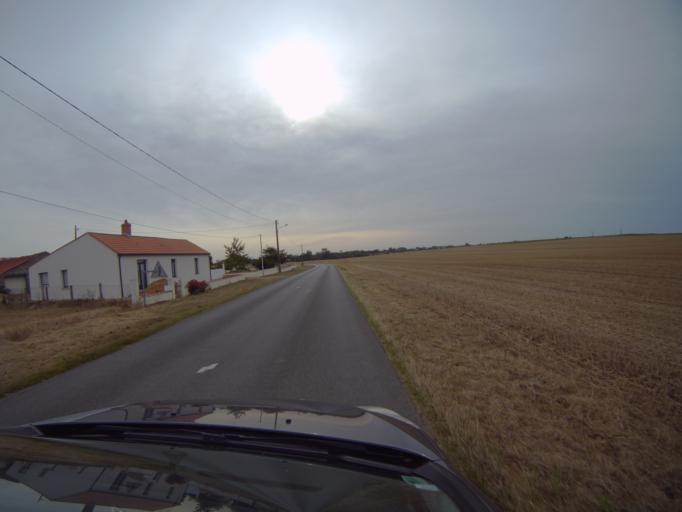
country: FR
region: Pays de la Loire
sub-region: Departement de la Vendee
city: Angles
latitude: 46.4069
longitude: -1.4299
